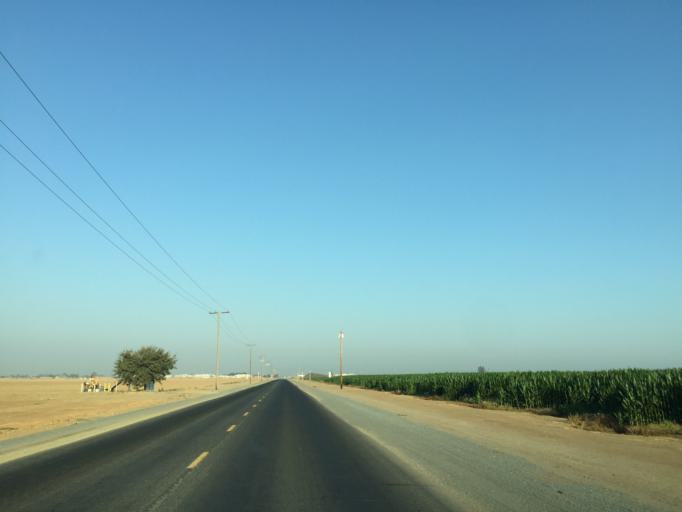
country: US
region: California
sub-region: Tulare County
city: Cutler
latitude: 36.4579
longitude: -119.3035
